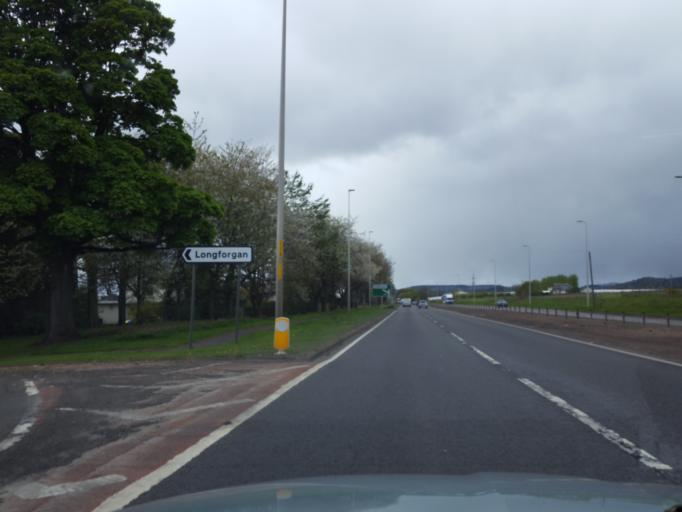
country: GB
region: Scotland
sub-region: Angus
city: Muirhead
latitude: 56.4593
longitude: -3.1110
